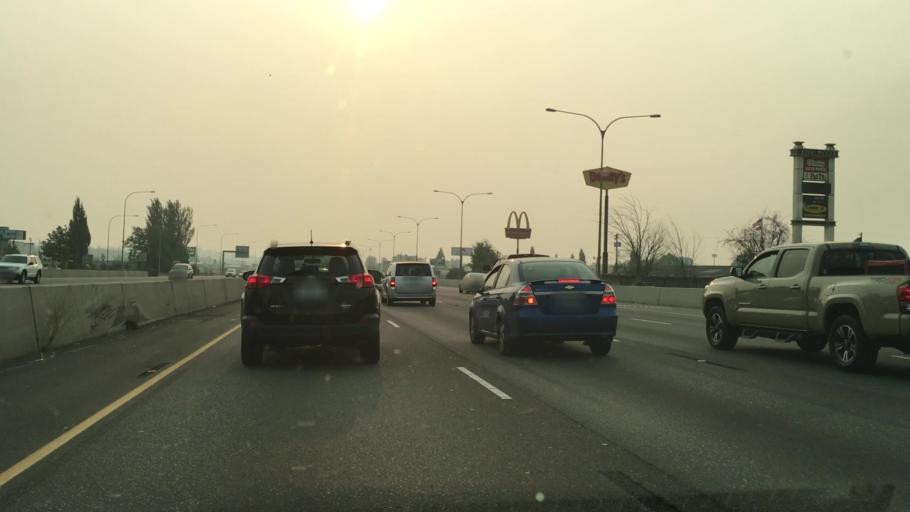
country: US
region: Washington
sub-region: Pierce County
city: Fife
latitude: 47.2400
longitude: -122.3582
